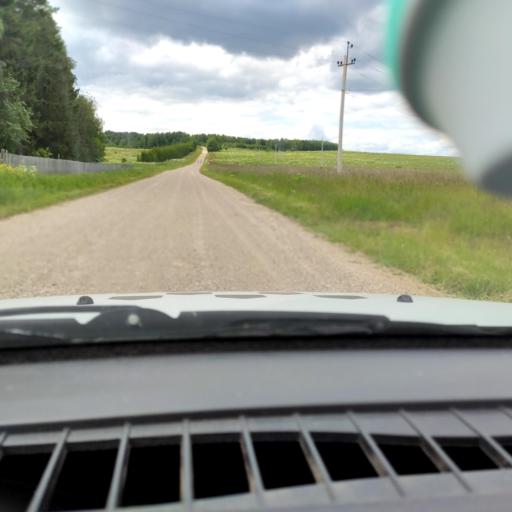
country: RU
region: Perm
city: Suksun
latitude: 57.2136
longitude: 57.6947
